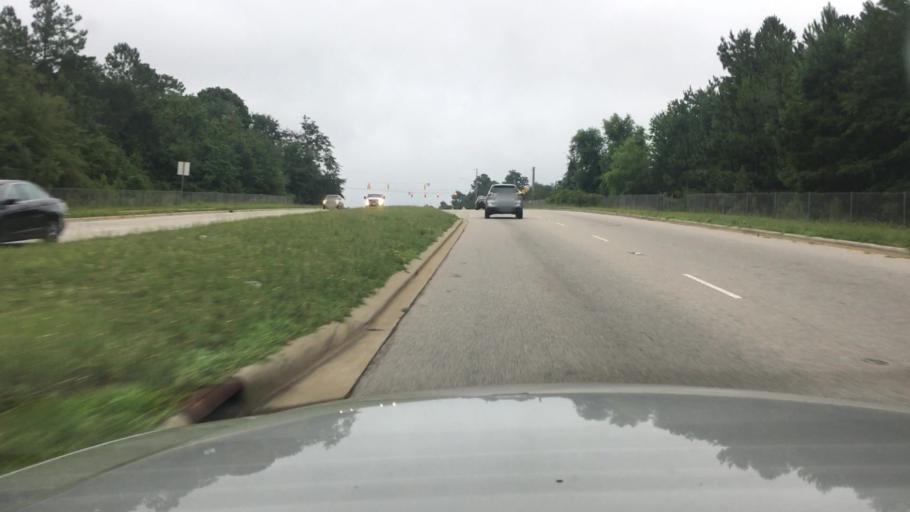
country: US
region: North Carolina
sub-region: Cumberland County
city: Hope Mills
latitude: 34.9850
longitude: -78.9327
